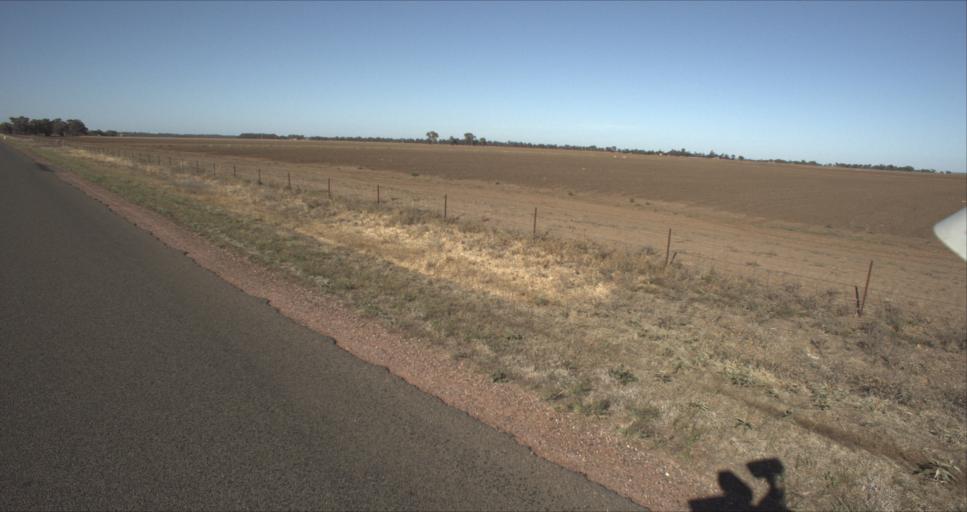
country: AU
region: New South Wales
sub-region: Leeton
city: Leeton
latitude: -34.5703
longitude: 146.2636
